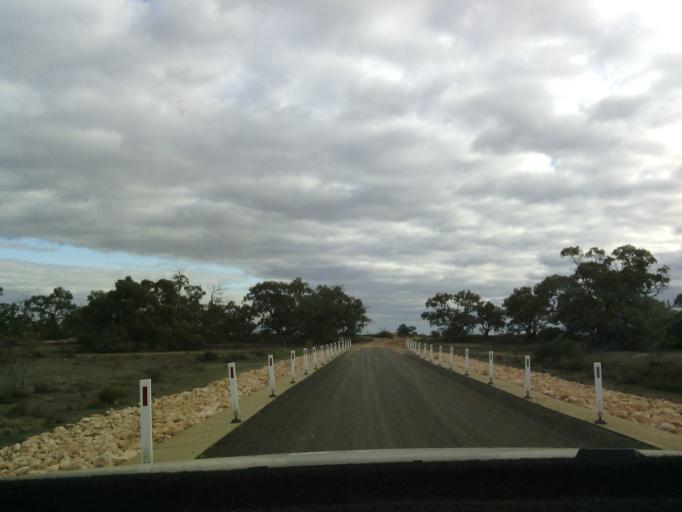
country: AU
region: South Australia
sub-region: Renmark Paringa
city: Renmark
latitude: -34.1681
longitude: 141.1831
